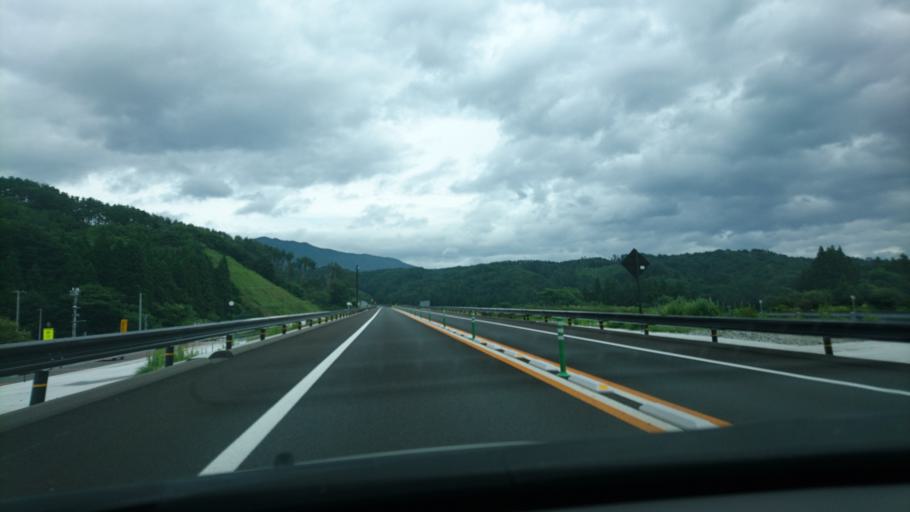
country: JP
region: Iwate
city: Yamada
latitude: 39.4801
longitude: 141.9481
